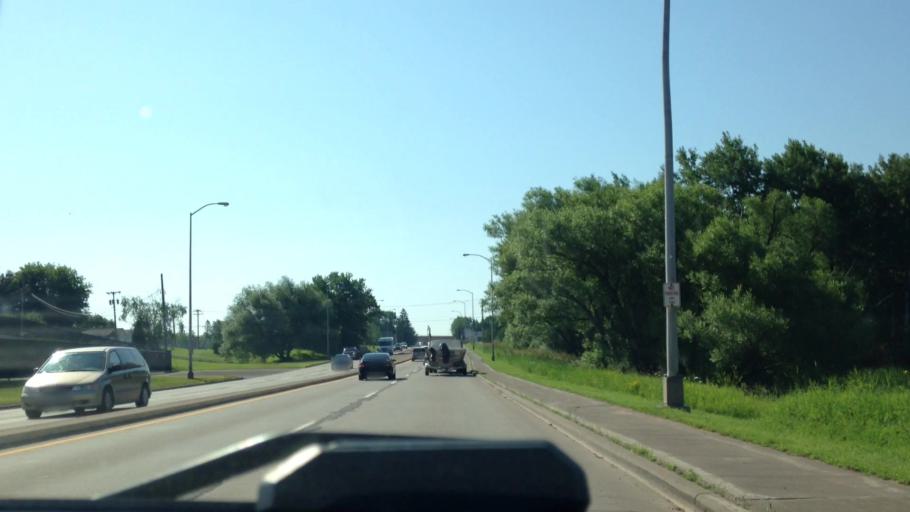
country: US
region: Wisconsin
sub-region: Douglas County
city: Superior
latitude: 46.6936
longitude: -92.0309
